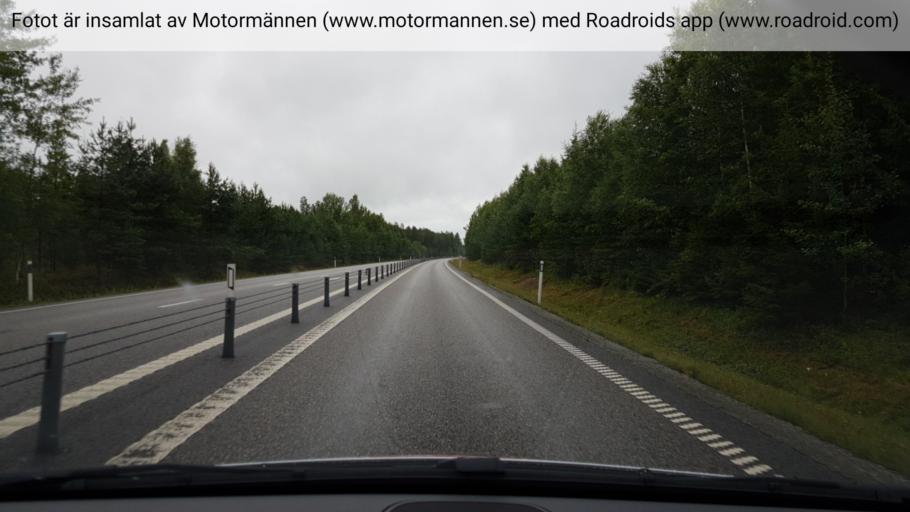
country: SE
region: Uppsala
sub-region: Heby Kommun
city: Tarnsjo
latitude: 60.1443
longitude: 16.9308
